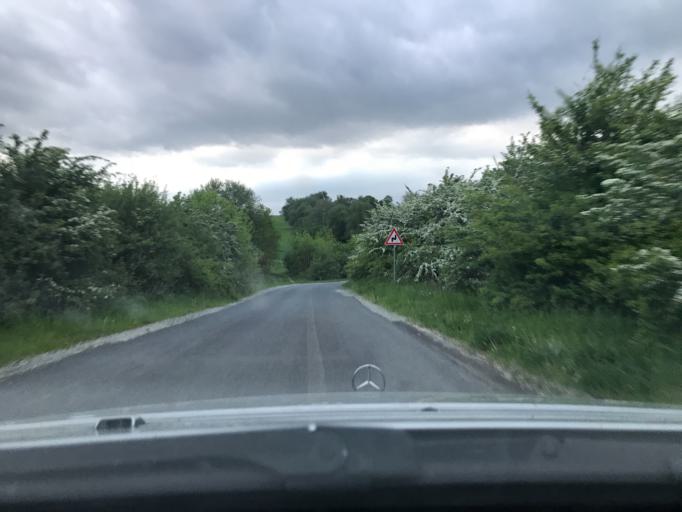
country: DE
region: Thuringia
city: Muehlhausen
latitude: 51.2160
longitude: 10.3986
